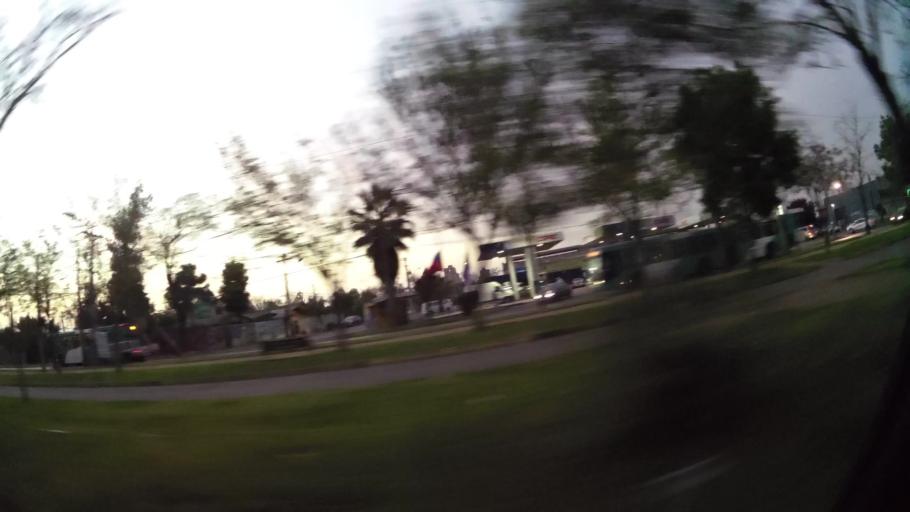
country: CL
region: Santiago Metropolitan
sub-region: Provincia de Santiago
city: Lo Prado
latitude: -33.4710
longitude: -70.7184
